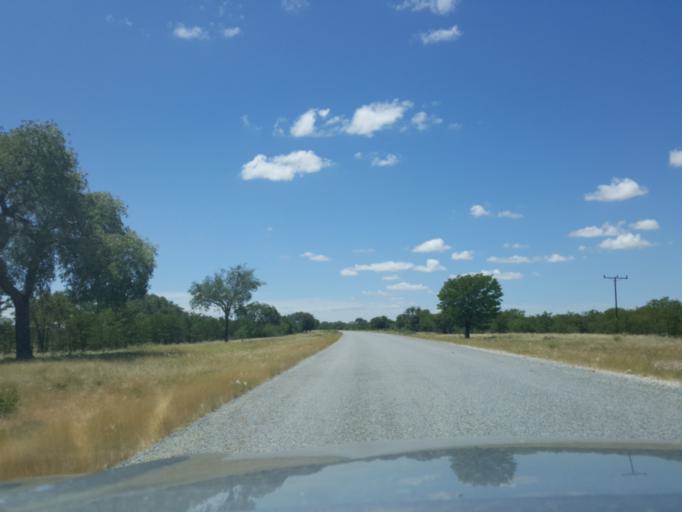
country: BW
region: Central
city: Nata
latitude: -20.1503
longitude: 25.7384
